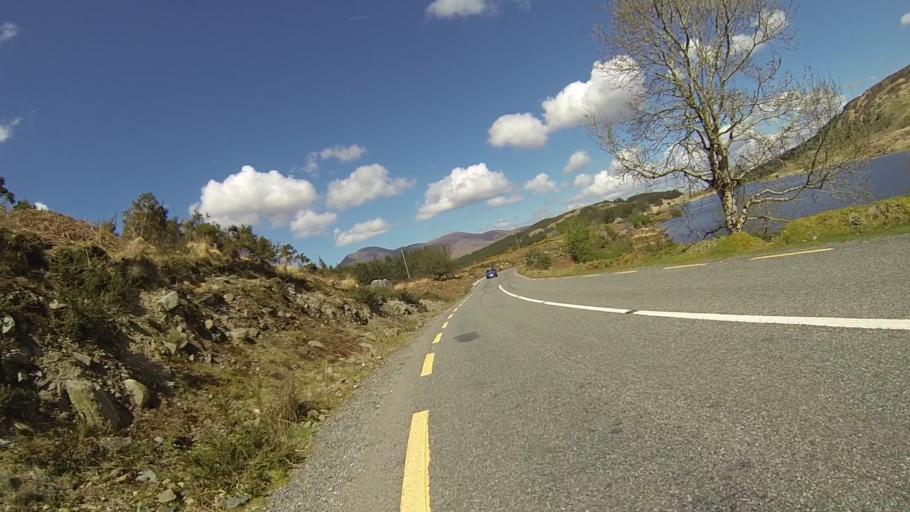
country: IE
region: Munster
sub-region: Ciarrai
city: Kenmare
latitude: 51.9528
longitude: -9.6271
